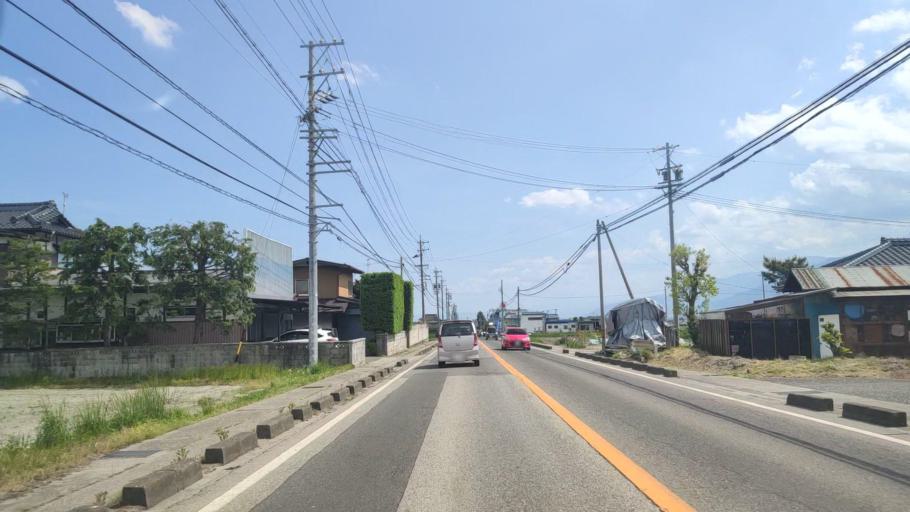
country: JP
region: Nagano
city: Omachi
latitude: 36.4573
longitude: 137.8511
